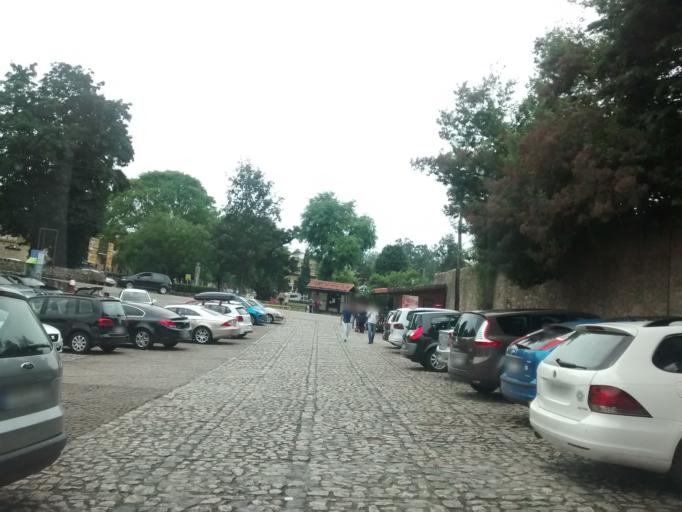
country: ES
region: Cantabria
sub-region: Provincia de Cantabria
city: Santillana
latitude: 43.3880
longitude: -4.1092
